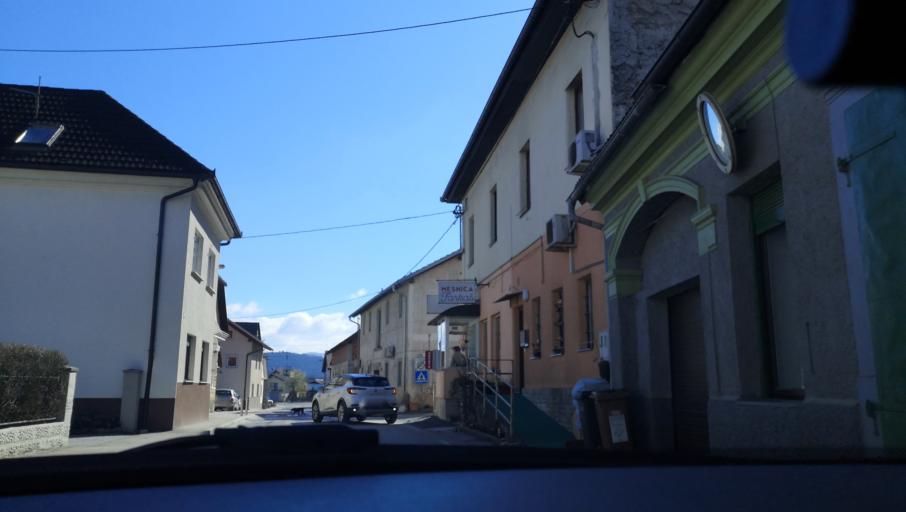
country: SI
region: Ig
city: Ig
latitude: 45.9597
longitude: 14.5255
